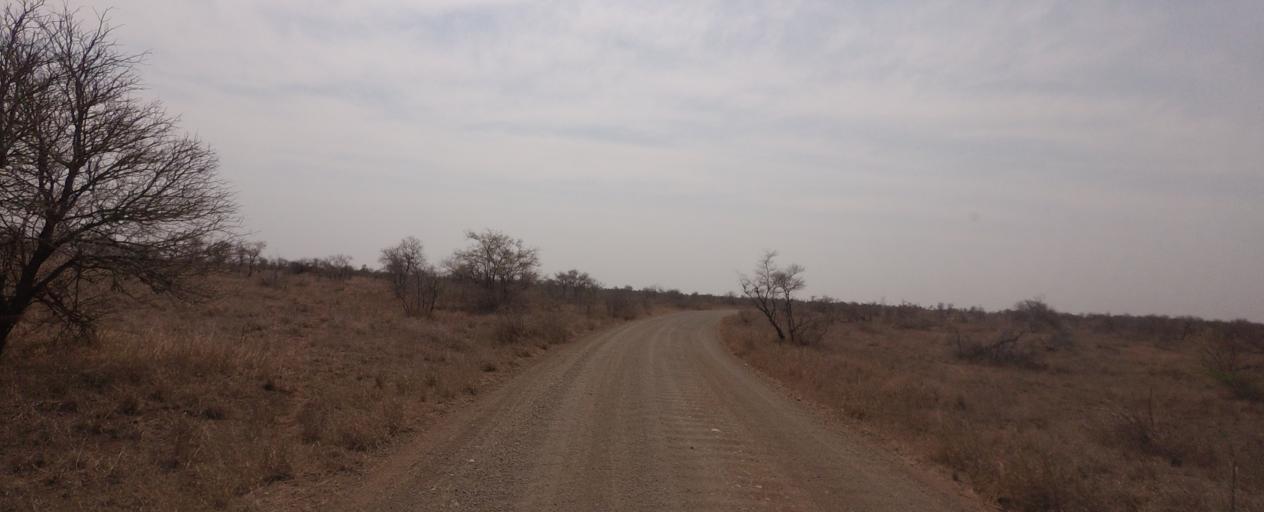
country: ZA
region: Limpopo
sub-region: Mopani District Municipality
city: Phalaborwa
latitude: -24.2603
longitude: 31.6648
